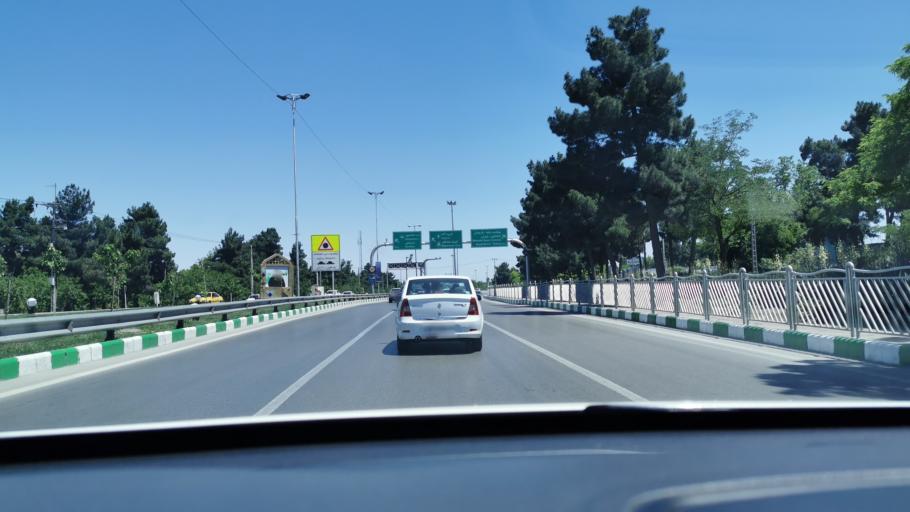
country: IR
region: Razavi Khorasan
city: Mashhad
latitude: 36.2536
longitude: 59.6038
